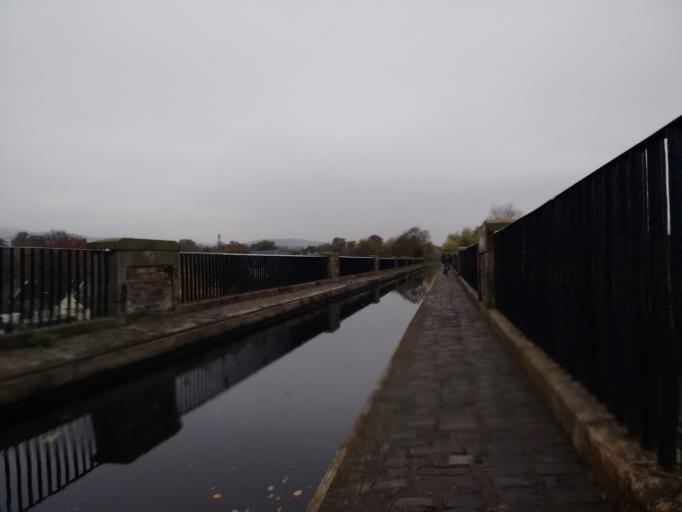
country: GB
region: Scotland
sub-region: Edinburgh
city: Colinton
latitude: 55.9238
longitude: -3.2488
